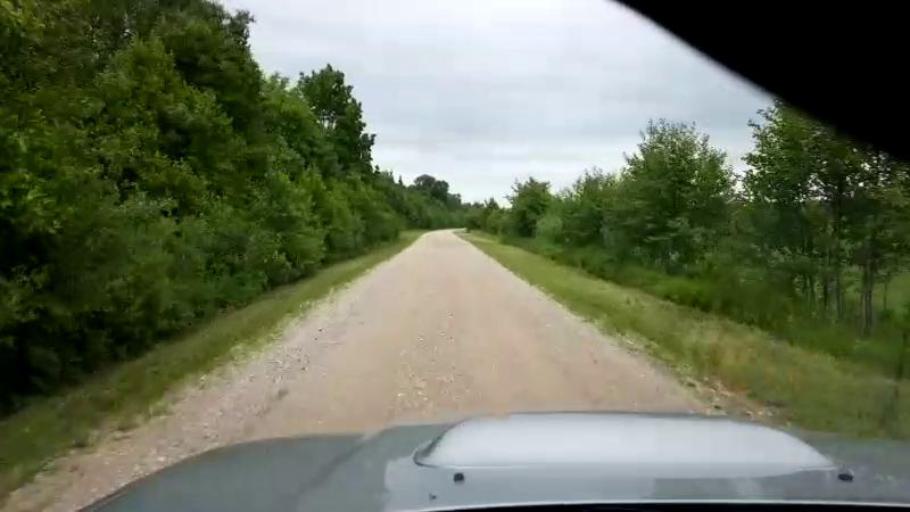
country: EE
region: Paernumaa
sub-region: Halinga vald
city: Parnu-Jaagupi
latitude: 58.5517
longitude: 24.5616
